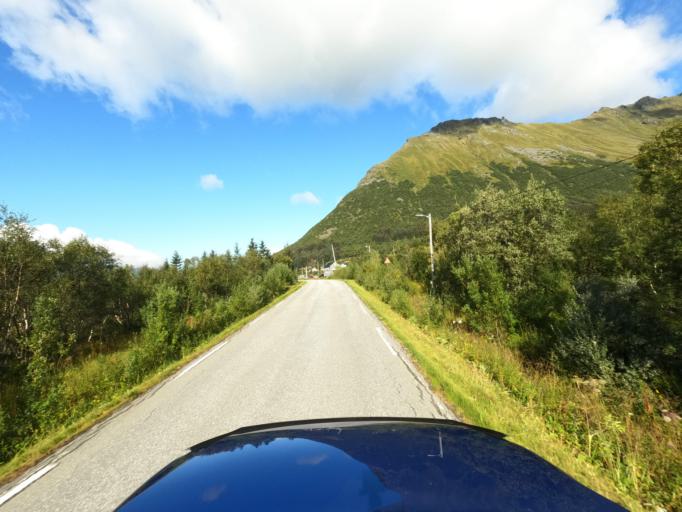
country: NO
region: Nordland
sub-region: Vagan
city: Kabelvag
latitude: 68.2844
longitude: 14.3482
